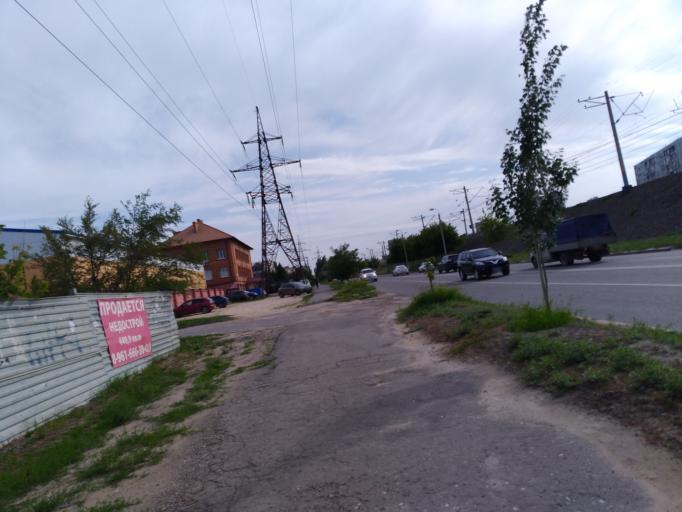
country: RU
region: Volgograd
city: Volgograd
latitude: 48.7044
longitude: 44.4944
